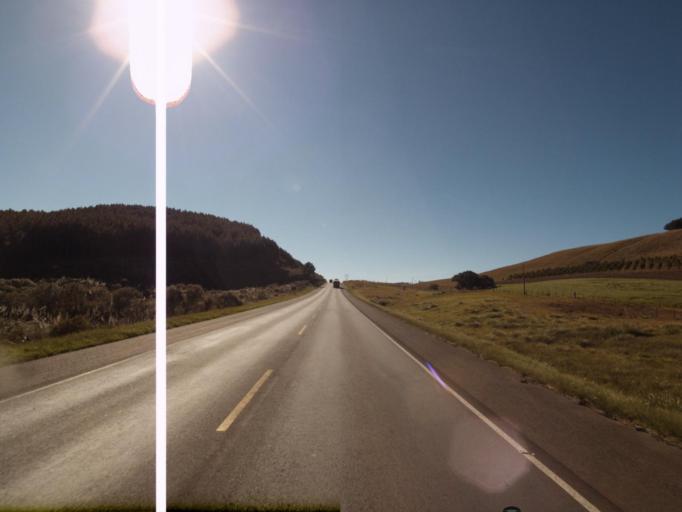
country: BR
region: Parana
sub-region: Palmas
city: Palmas
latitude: -26.6588
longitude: -51.5375
